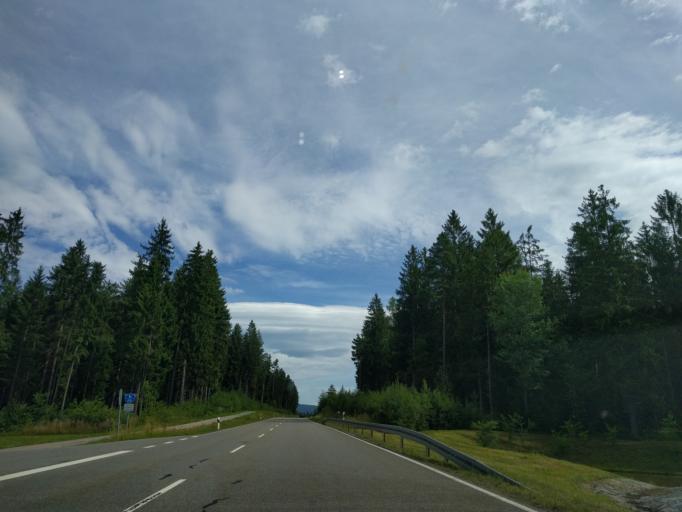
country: DE
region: Bavaria
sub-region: Lower Bavaria
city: Langdorf
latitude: 48.9945
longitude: 13.1369
